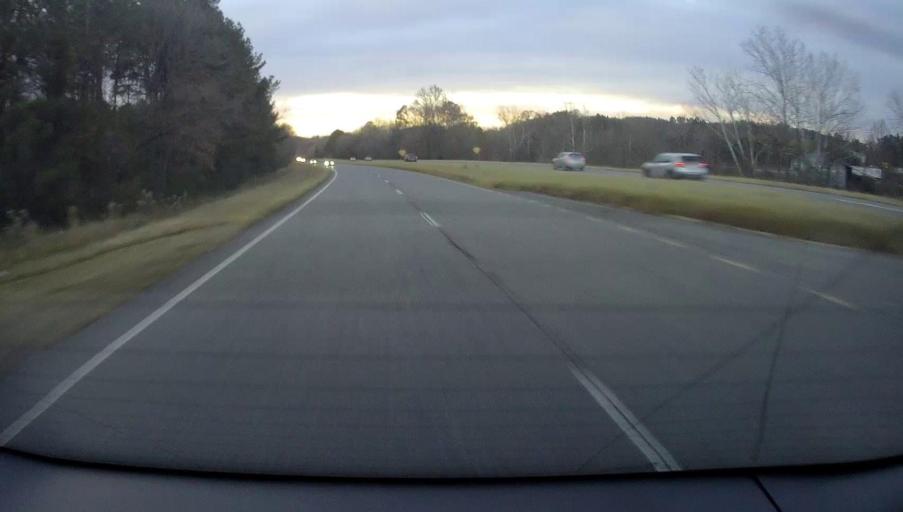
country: US
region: Alabama
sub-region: Etowah County
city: Glencoe
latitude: 33.9417
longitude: -85.9175
